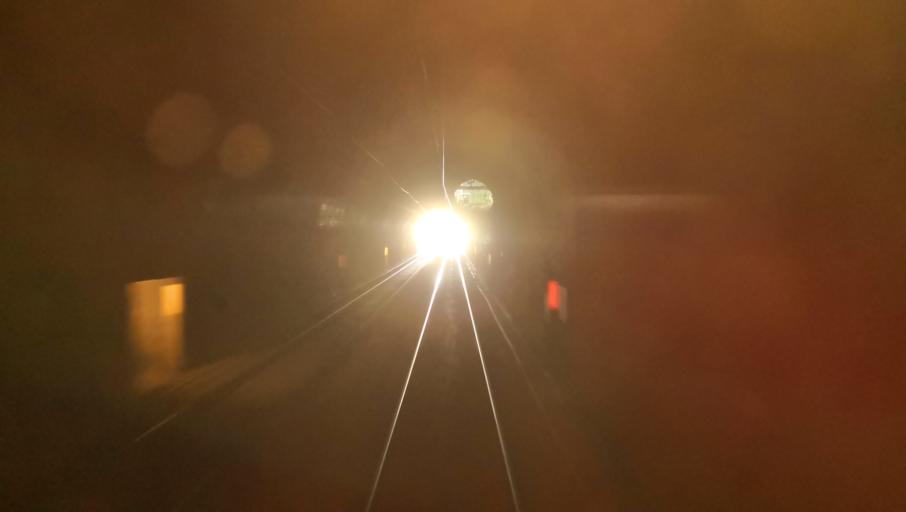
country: FR
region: Haute-Normandie
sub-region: Departement de l'Eure
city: Bernay
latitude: 49.0869
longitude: 0.5919
